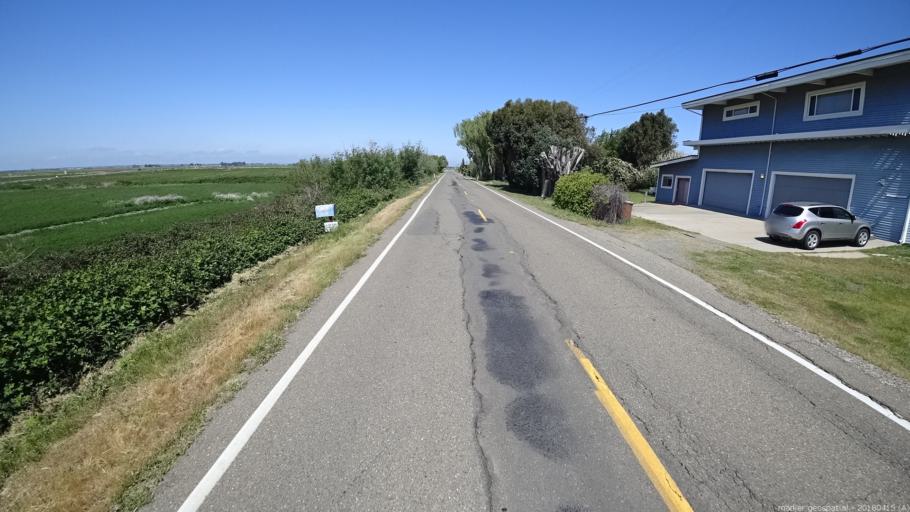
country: US
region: California
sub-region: Solano County
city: Rio Vista
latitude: 38.1321
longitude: -121.5914
